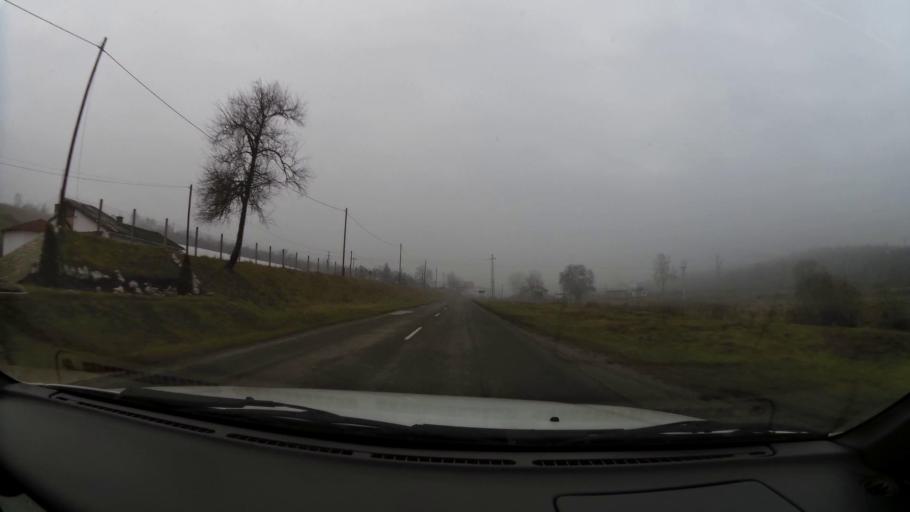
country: HU
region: Borsod-Abauj-Zemplen
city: Rudabanya
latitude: 48.3655
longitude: 20.6296
